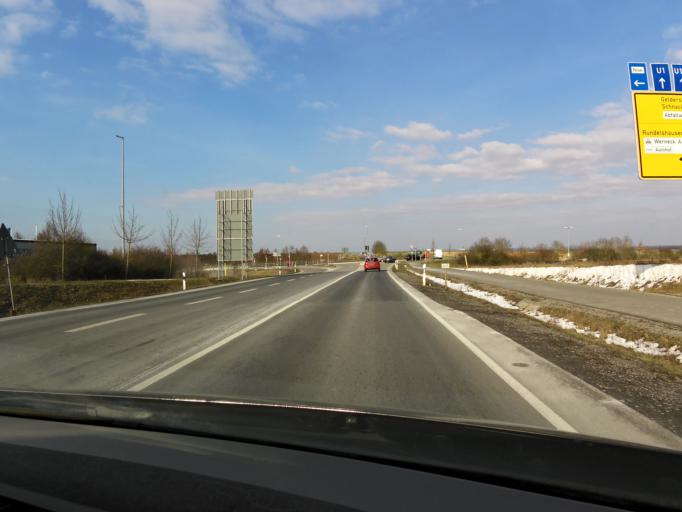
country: DE
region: Bavaria
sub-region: Regierungsbezirk Unterfranken
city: Werneck
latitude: 50.0032
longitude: 10.1200
